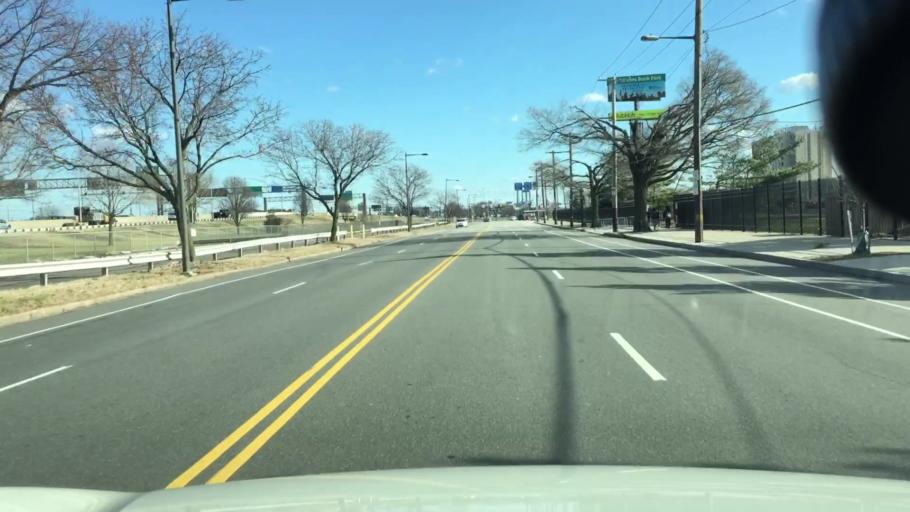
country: US
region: Pennsylvania
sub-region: Philadelphia County
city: Philadelphia
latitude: 39.9113
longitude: -75.1695
